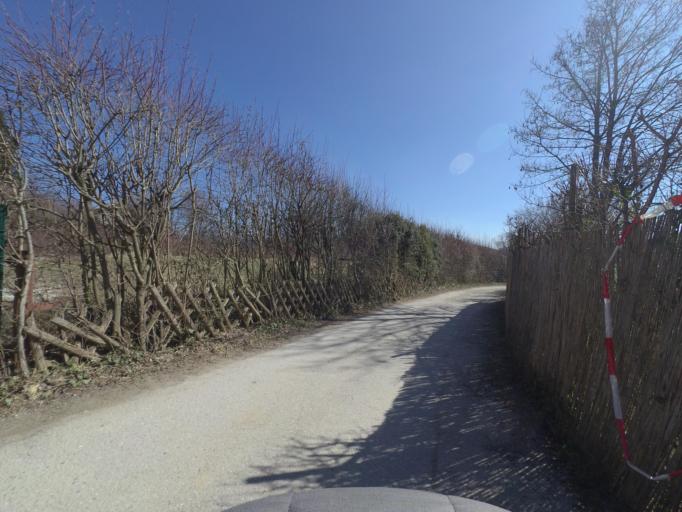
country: AT
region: Salzburg
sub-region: Politischer Bezirk Salzburg-Umgebung
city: Mattsee
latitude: 47.9879
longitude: 13.1152
